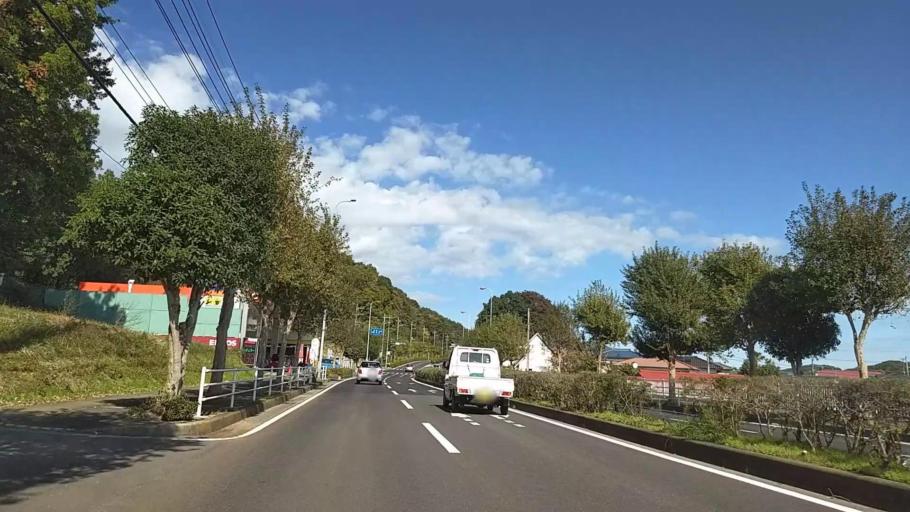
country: JP
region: Kanagawa
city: Hadano
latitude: 35.3420
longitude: 139.2303
